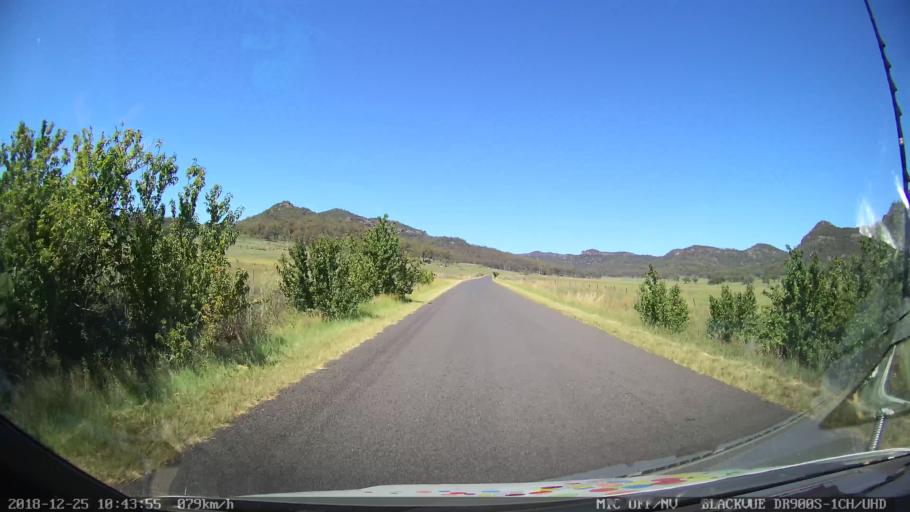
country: AU
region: New South Wales
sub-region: Upper Hunter Shire
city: Merriwa
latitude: -32.4251
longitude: 150.3070
